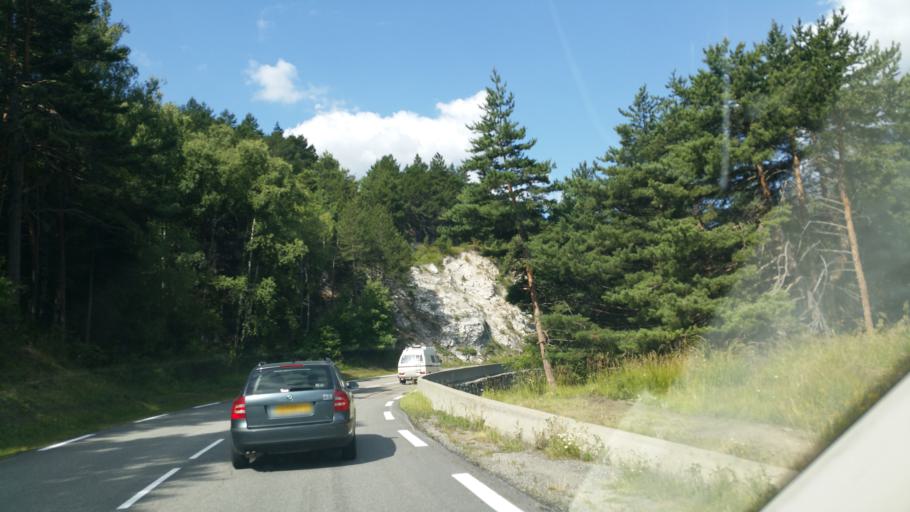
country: FR
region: Rhone-Alpes
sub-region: Departement de la Savoie
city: Modane
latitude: 45.2101
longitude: 6.7211
